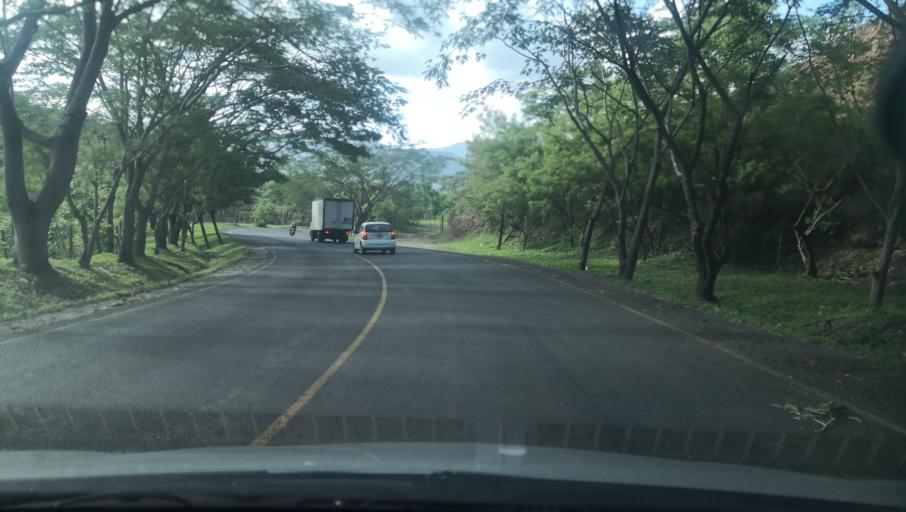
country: NI
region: Madriz
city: Totogalpa
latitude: 13.5923
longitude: -86.4721
